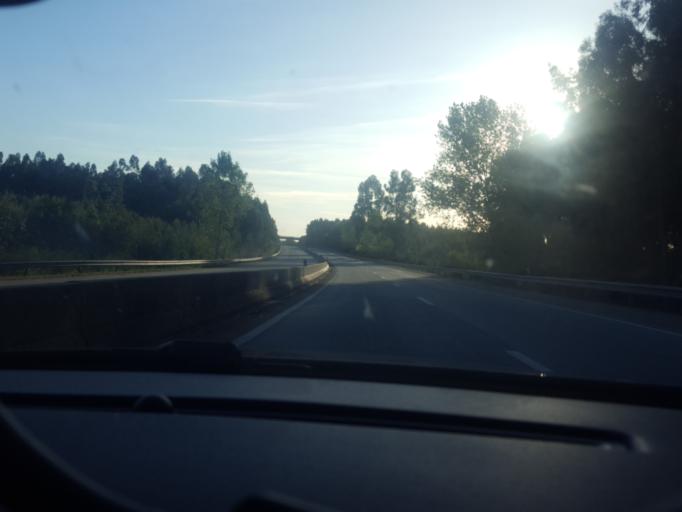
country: PT
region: Viseu
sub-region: Concelho de Carregal do Sal
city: Carregal do Sal
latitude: 40.4152
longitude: -8.0512
